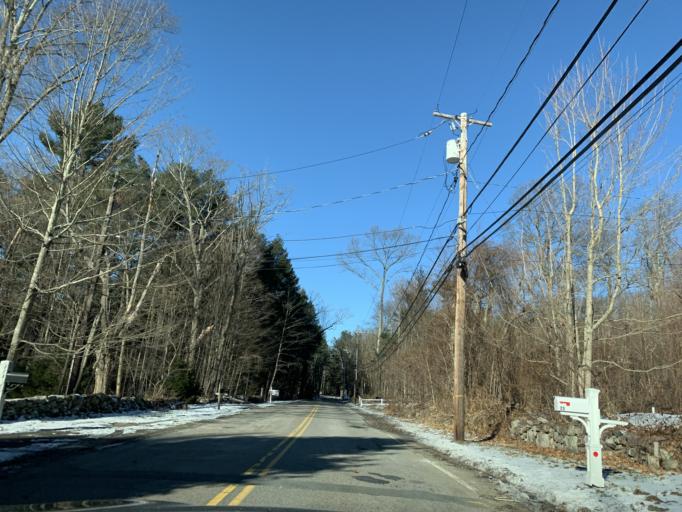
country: US
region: Massachusetts
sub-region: Norfolk County
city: Canton
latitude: 42.1951
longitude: -71.1199
